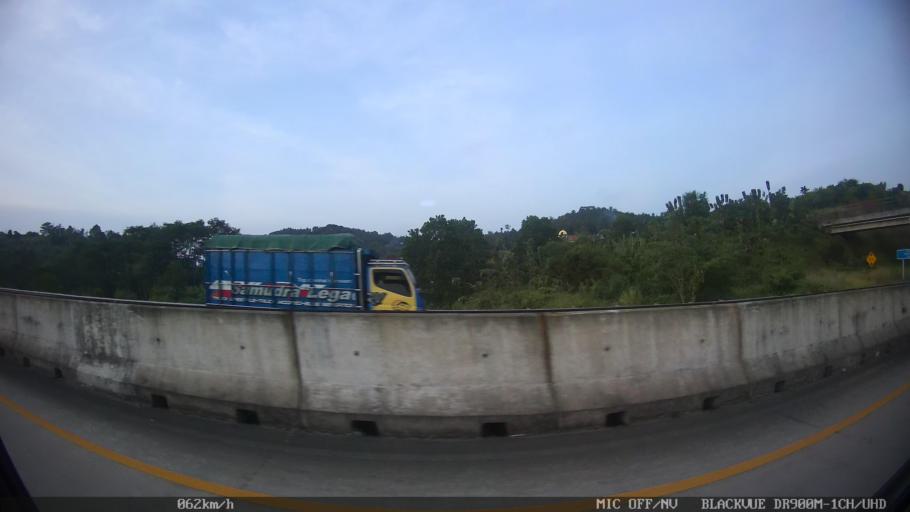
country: ID
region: Lampung
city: Penengahan
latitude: -5.8597
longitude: 105.7332
